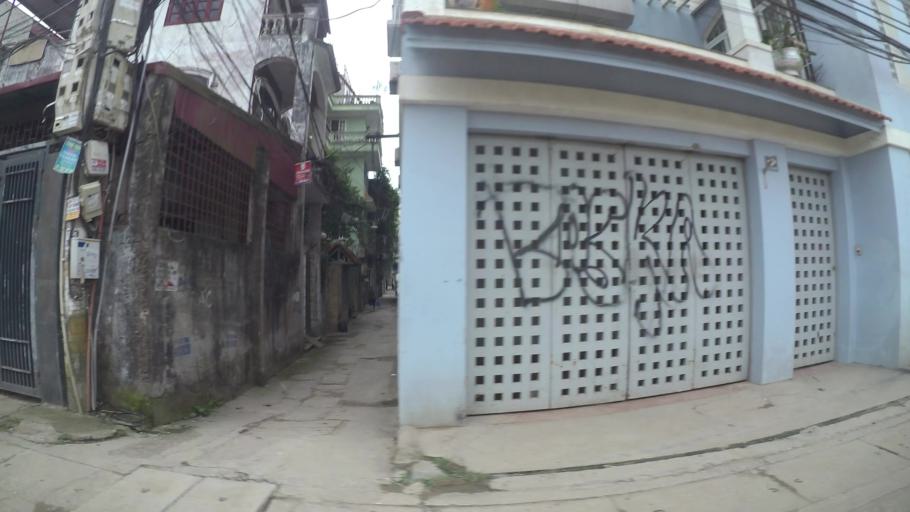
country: VN
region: Ha Noi
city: Tay Ho
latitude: 21.0675
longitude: 105.8350
